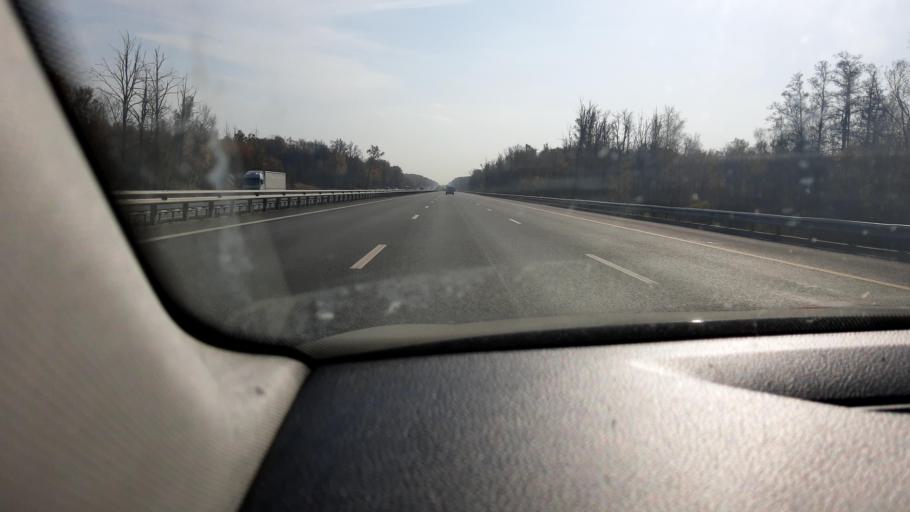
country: RU
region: Moskovskaya
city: Stupino
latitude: 54.9279
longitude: 37.9967
